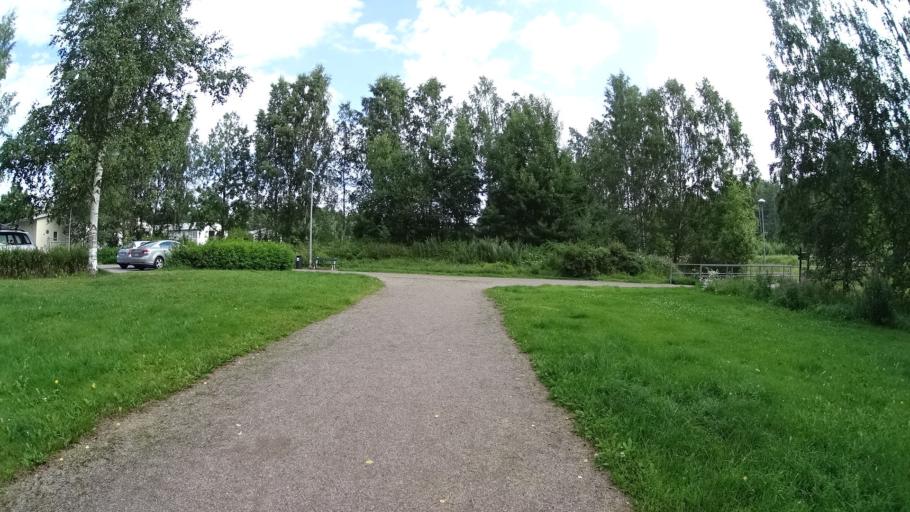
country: FI
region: Uusimaa
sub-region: Helsinki
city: Kilo
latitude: 60.2322
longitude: 24.7846
